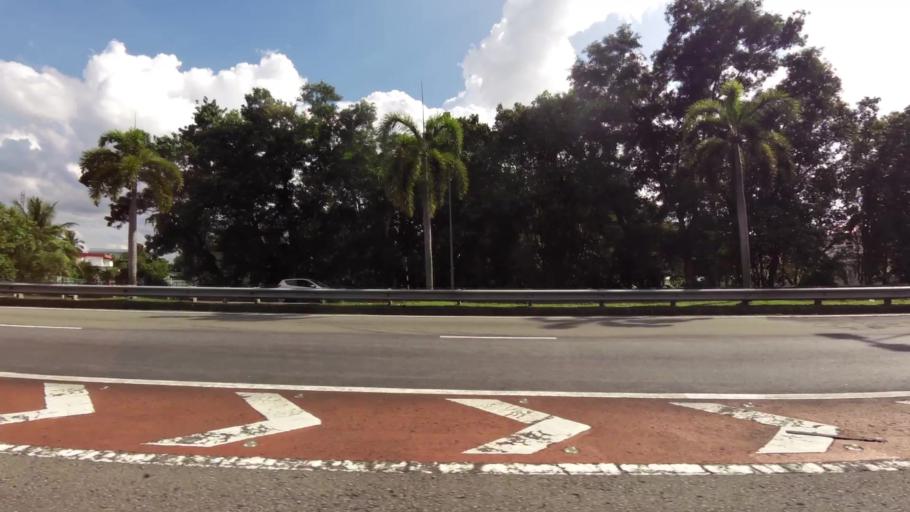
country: BN
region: Brunei and Muara
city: Bandar Seri Begawan
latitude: 4.9513
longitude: 114.9615
